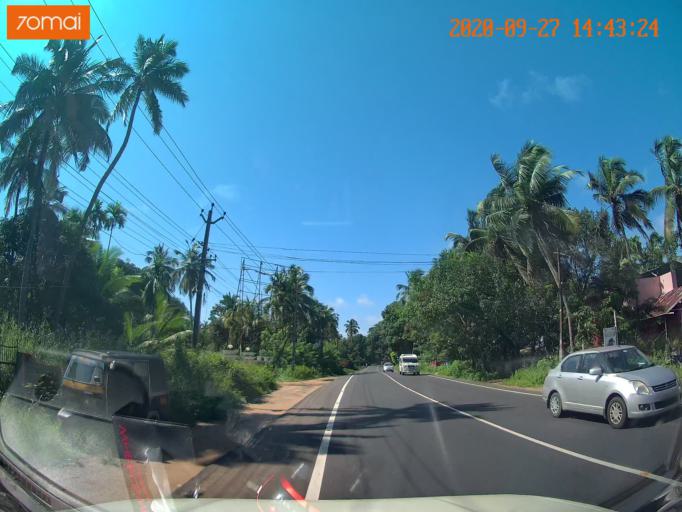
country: IN
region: Kerala
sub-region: Thrissur District
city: Thanniyam
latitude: 10.4428
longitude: 76.0933
